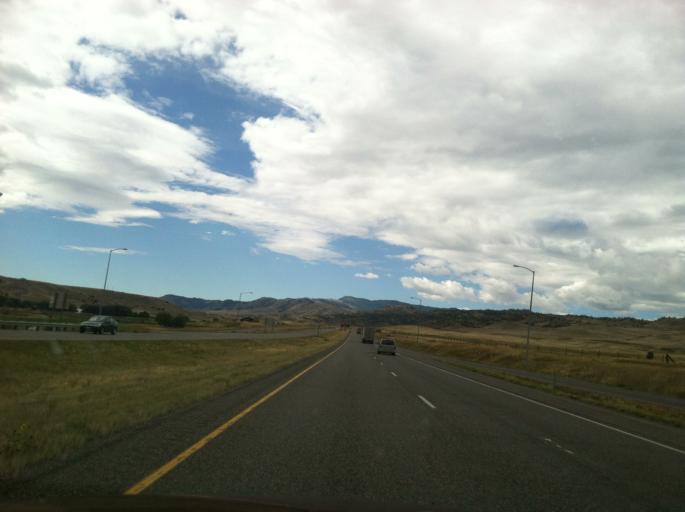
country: US
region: Montana
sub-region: Park County
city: Livingston
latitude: 45.6524
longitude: -110.6153
